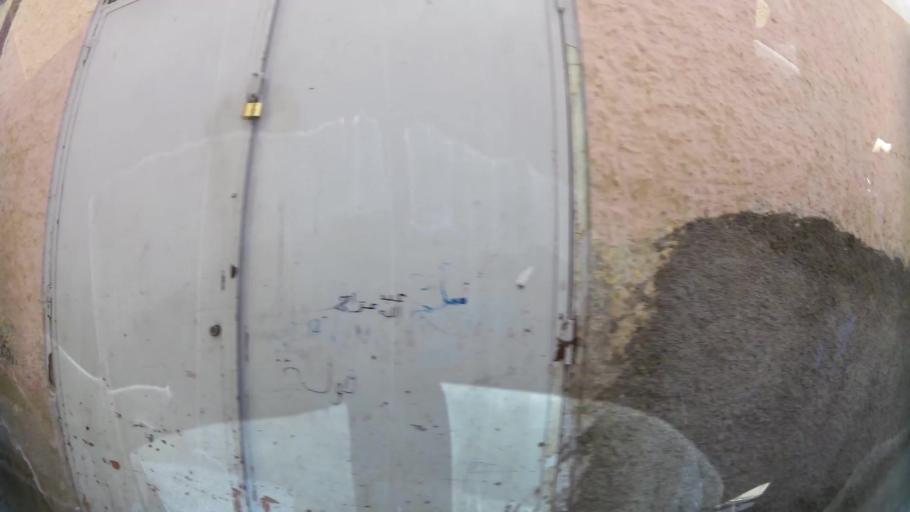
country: MA
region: Oriental
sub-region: Oujda-Angad
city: Oujda
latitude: 34.6722
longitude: -1.9282
